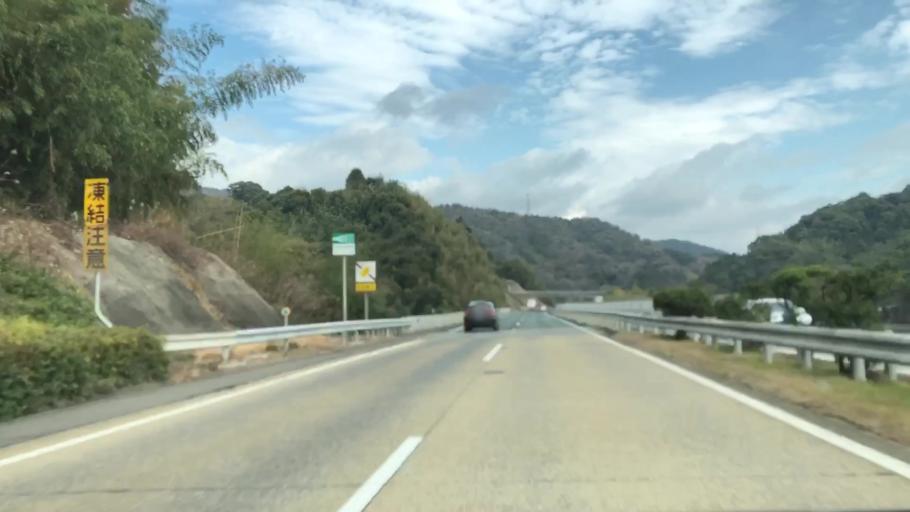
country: JP
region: Saga Prefecture
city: Kanzakimachi-kanzaki
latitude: 33.3351
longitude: 130.3263
